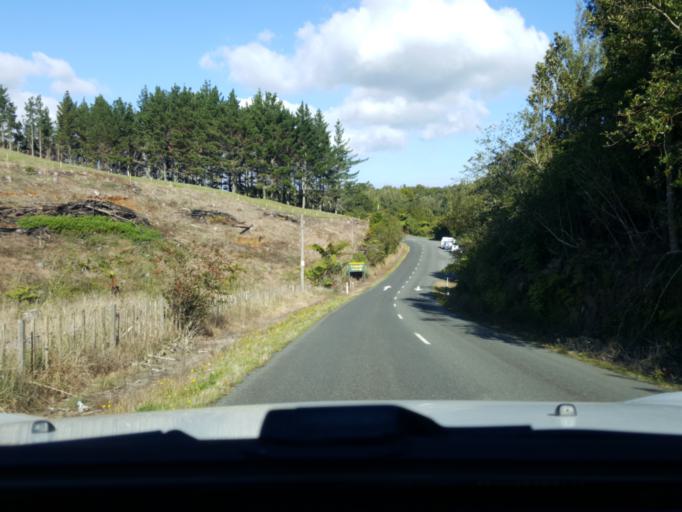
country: NZ
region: Waikato
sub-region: Waikato District
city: Raglan
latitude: -37.9061
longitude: 174.9013
